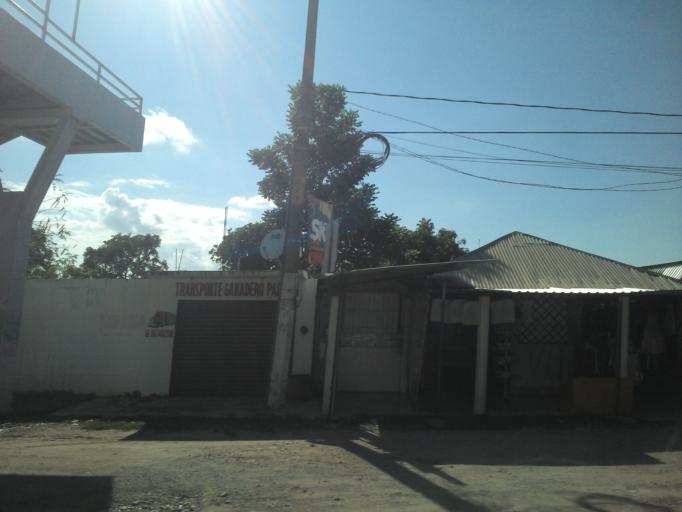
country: MX
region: Chiapas
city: Palenque
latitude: 17.5398
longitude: -91.9914
